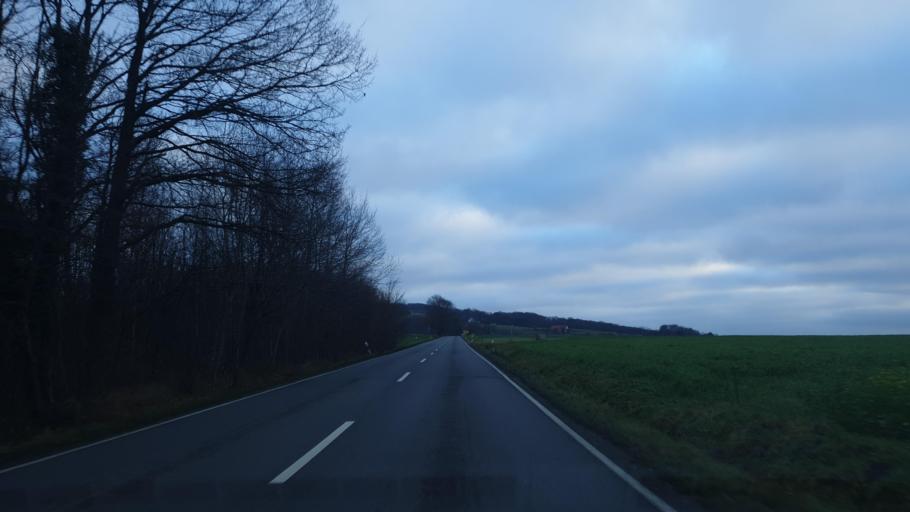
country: DE
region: North Rhine-Westphalia
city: Loehne
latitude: 52.1657
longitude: 8.6832
